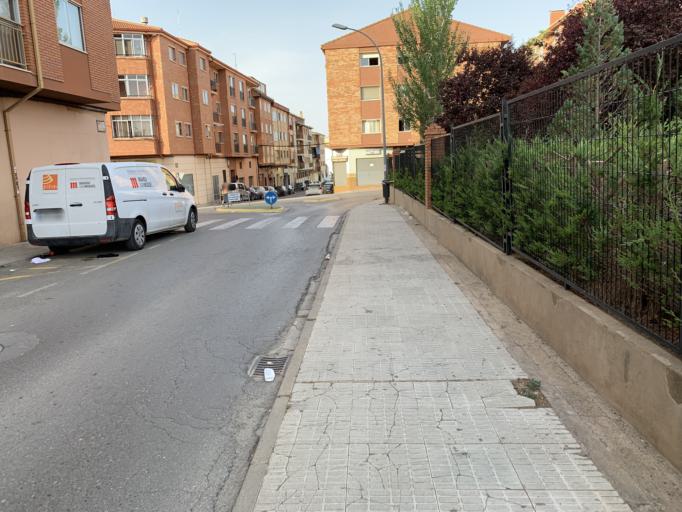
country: ES
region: Aragon
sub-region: Provincia de Teruel
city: Teruel
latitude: 40.3497
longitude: -1.1113
